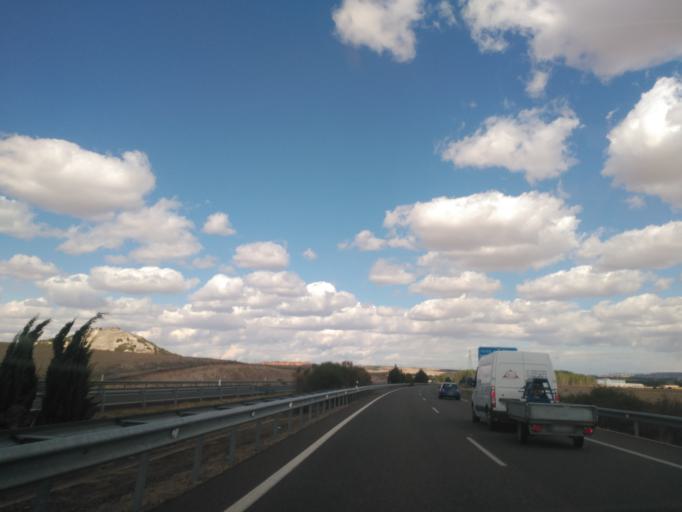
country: ES
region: Castille and Leon
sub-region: Provincia de Palencia
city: Soto de Cerrato
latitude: 41.9737
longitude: -4.4502
